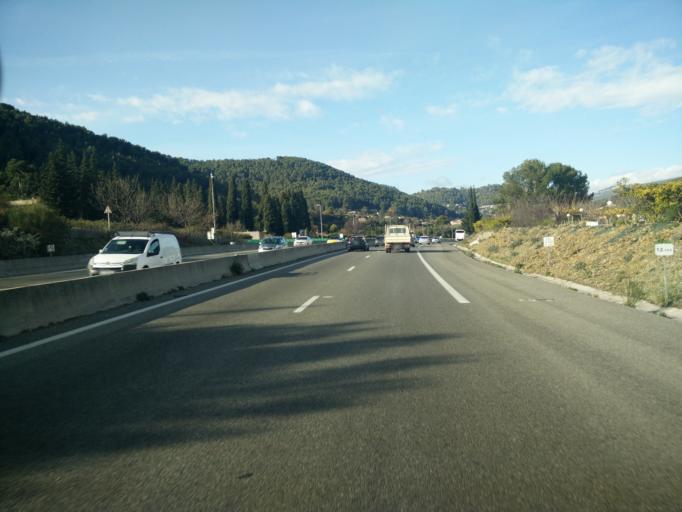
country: FR
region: Provence-Alpes-Cote d'Azur
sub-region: Departement du Var
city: Sollies-Pont
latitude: 43.1876
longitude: 6.0386
